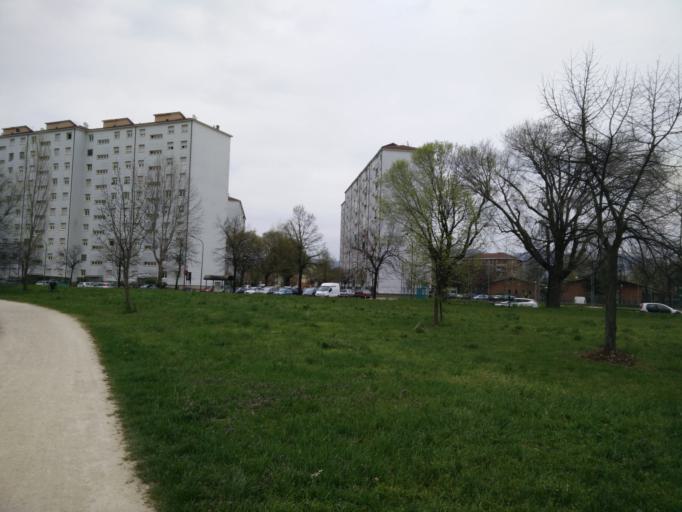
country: IT
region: Piedmont
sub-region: Provincia di Torino
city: Nichelino
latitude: 45.0101
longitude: 7.6489
